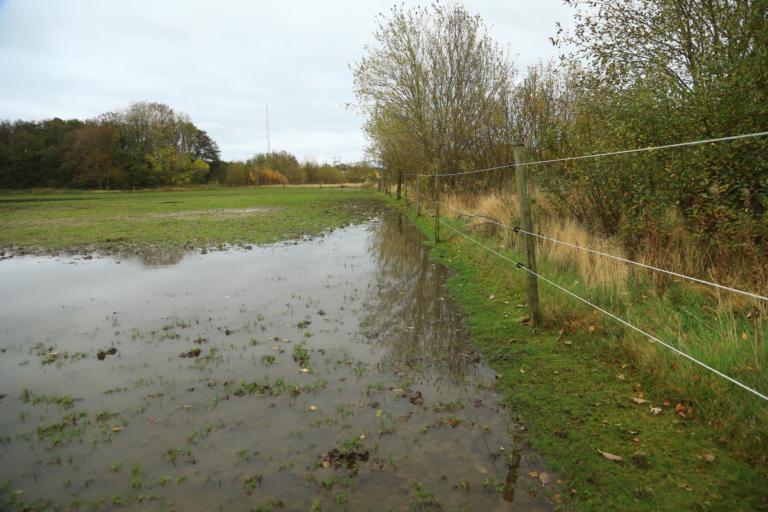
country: SE
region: Halland
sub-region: Varbergs Kommun
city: Varberg
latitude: 57.1265
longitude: 12.2978
